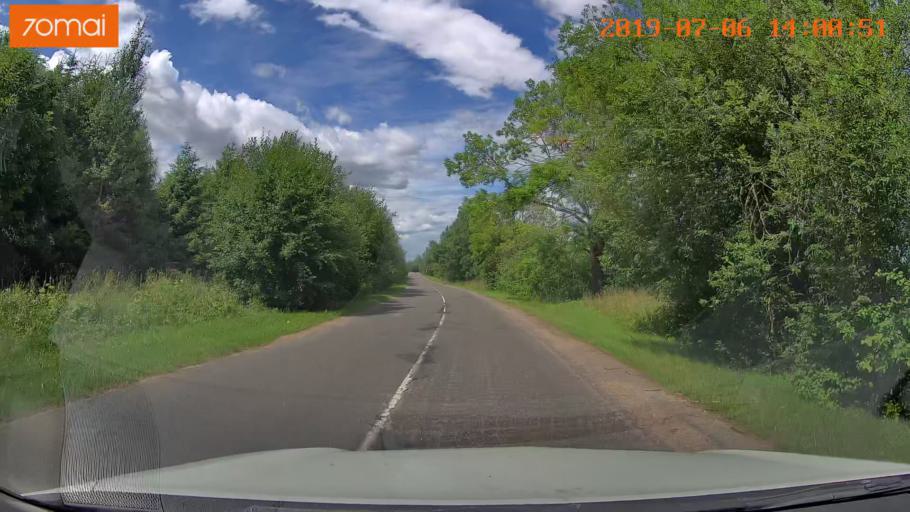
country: BY
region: Minsk
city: Ivyanyets
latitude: 53.8026
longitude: 26.8186
